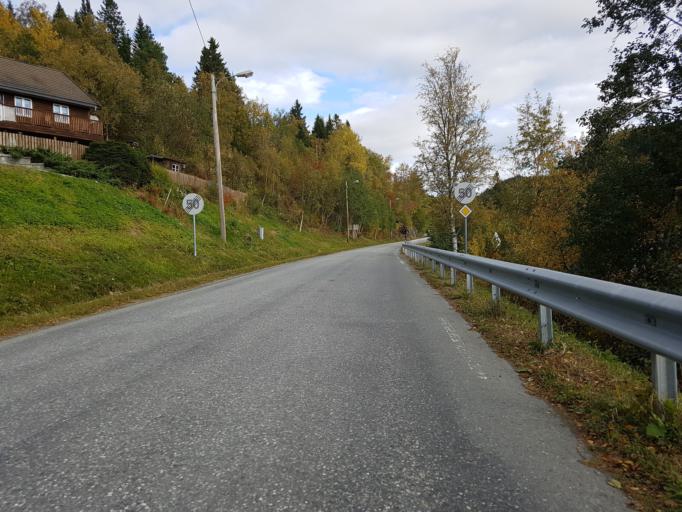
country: NO
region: Sor-Trondelag
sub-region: Klaebu
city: Klaebu
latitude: 63.3973
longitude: 10.5475
